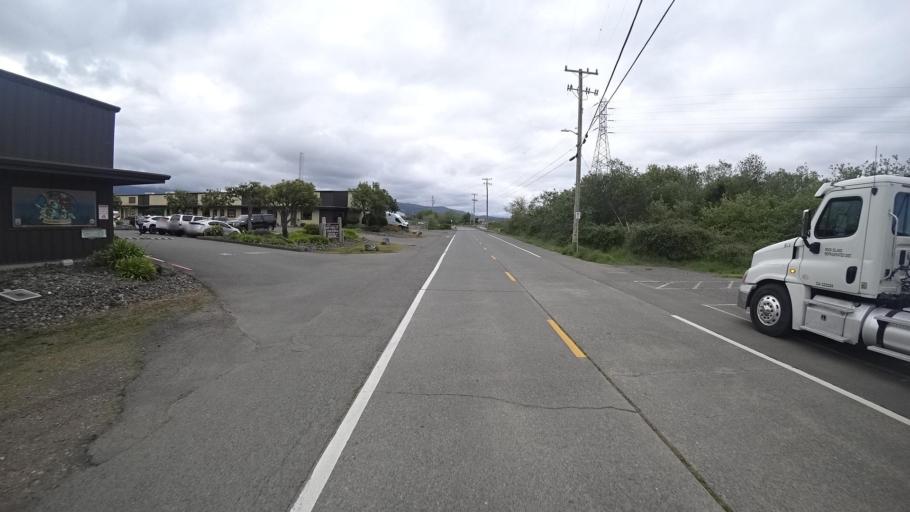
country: US
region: California
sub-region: Humboldt County
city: Arcata
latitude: 40.8571
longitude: -124.0897
